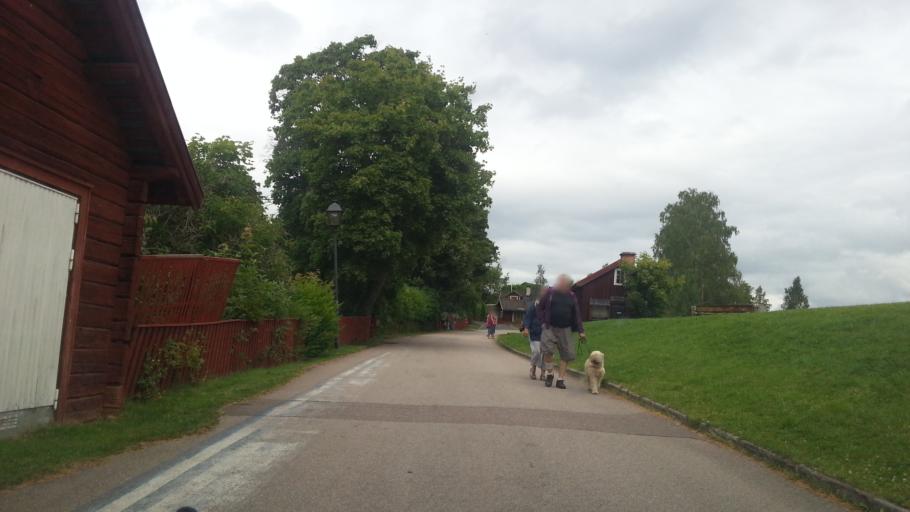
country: SE
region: Dalarna
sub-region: Faluns Kommun
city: Falun
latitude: 60.6512
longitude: 15.7762
